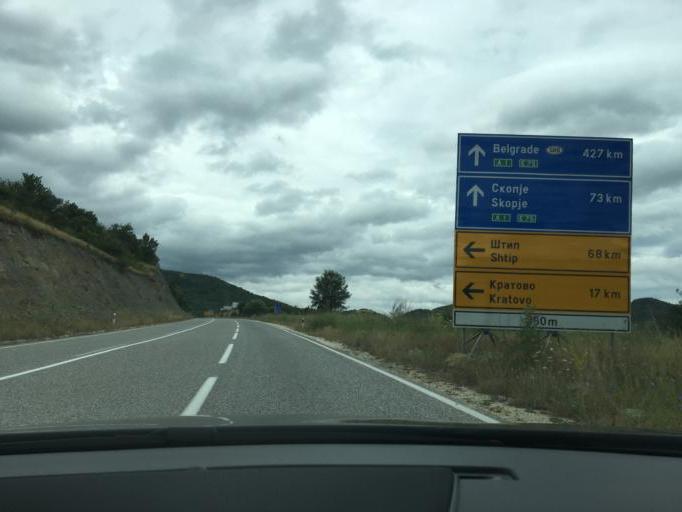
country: MK
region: Opstina Rankovce
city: Rankovce
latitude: 42.1587
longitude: 22.0571
